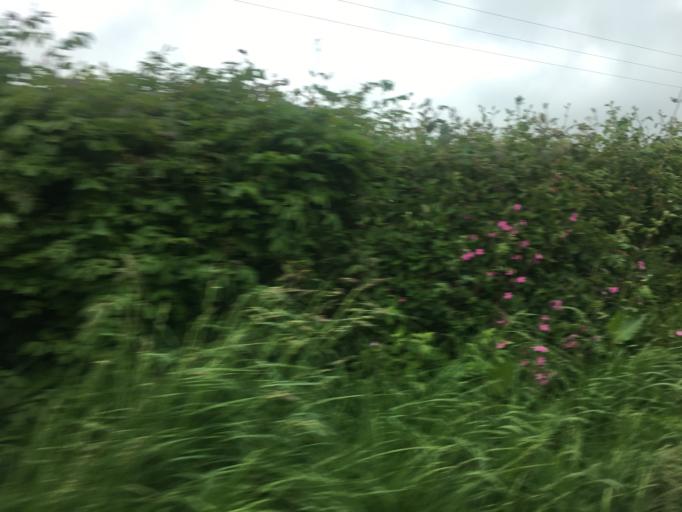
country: GB
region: Wales
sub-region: County of Ceredigion
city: Lampeter
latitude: 52.0811
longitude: -4.0442
